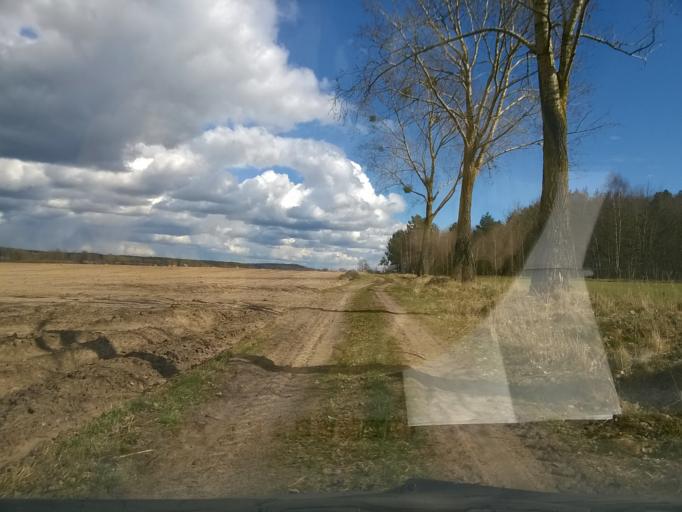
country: PL
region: Kujawsko-Pomorskie
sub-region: Powiat nakielski
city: Kcynia
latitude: 53.0331
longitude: 17.4098
